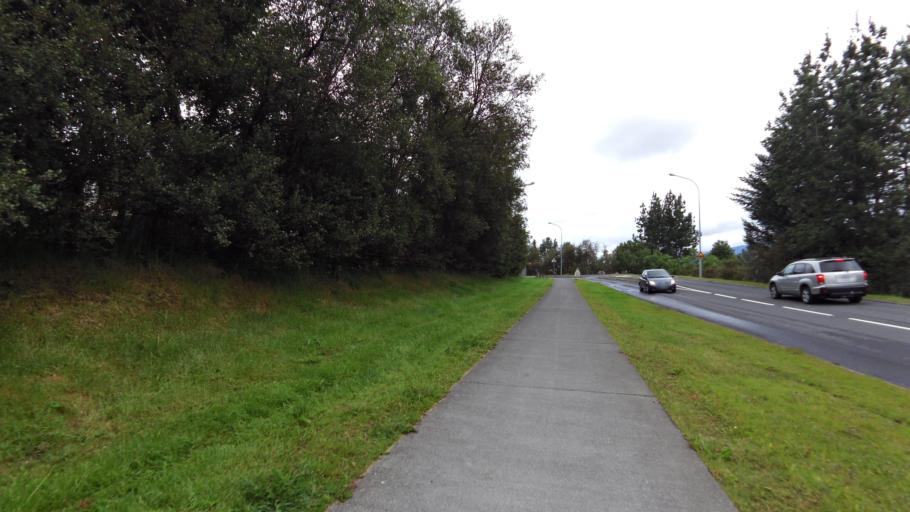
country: IS
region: Capital Region
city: Reykjavik
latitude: 64.1216
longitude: -21.8541
